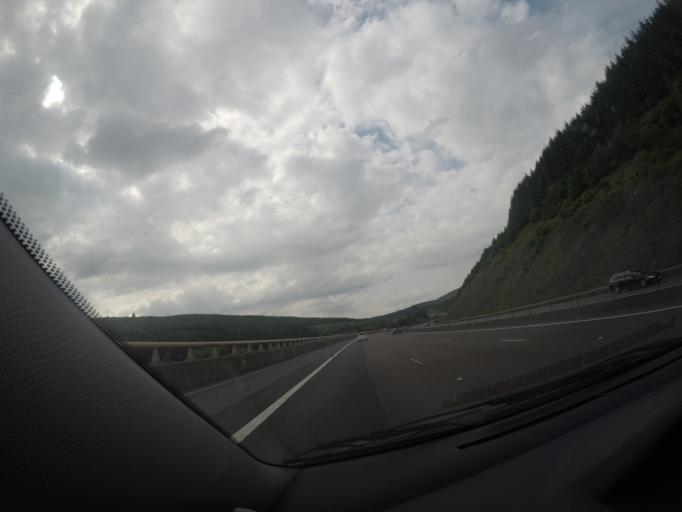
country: GB
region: Scotland
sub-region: Dumfries and Galloway
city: Moffat
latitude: 55.4007
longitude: -3.5515
